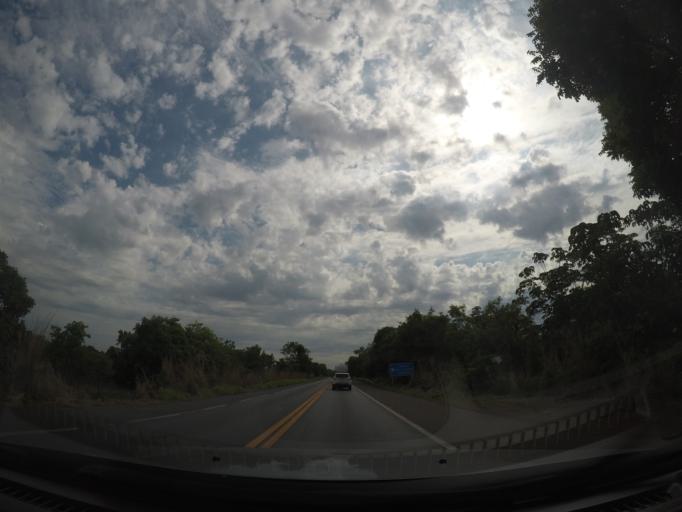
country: BR
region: Goias
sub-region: Formosa
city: Formosa
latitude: -14.9183
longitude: -46.9582
